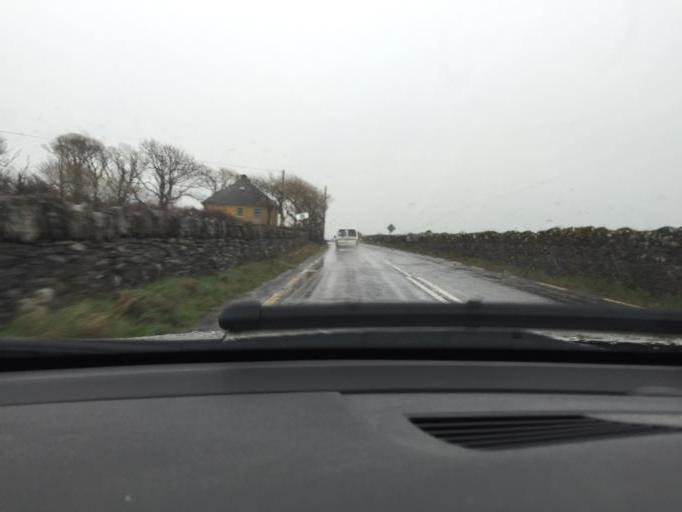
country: IE
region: Munster
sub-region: Ciarrai
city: Dingle
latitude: 52.1298
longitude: -10.2504
